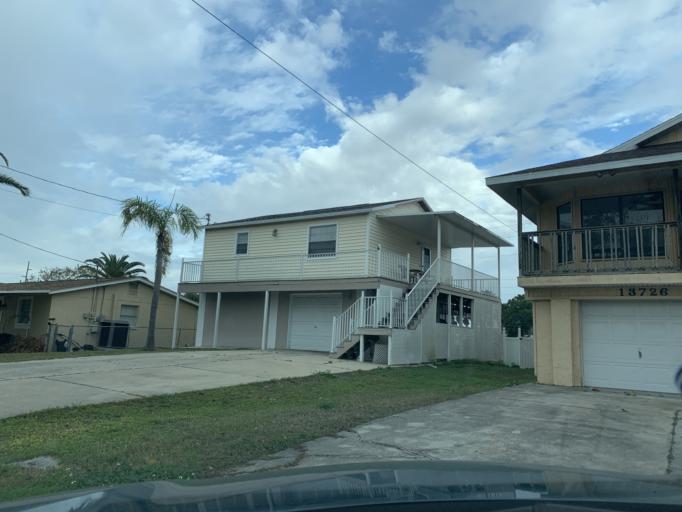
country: US
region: Florida
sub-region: Pasco County
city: Hudson
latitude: 28.3572
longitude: -82.6999
